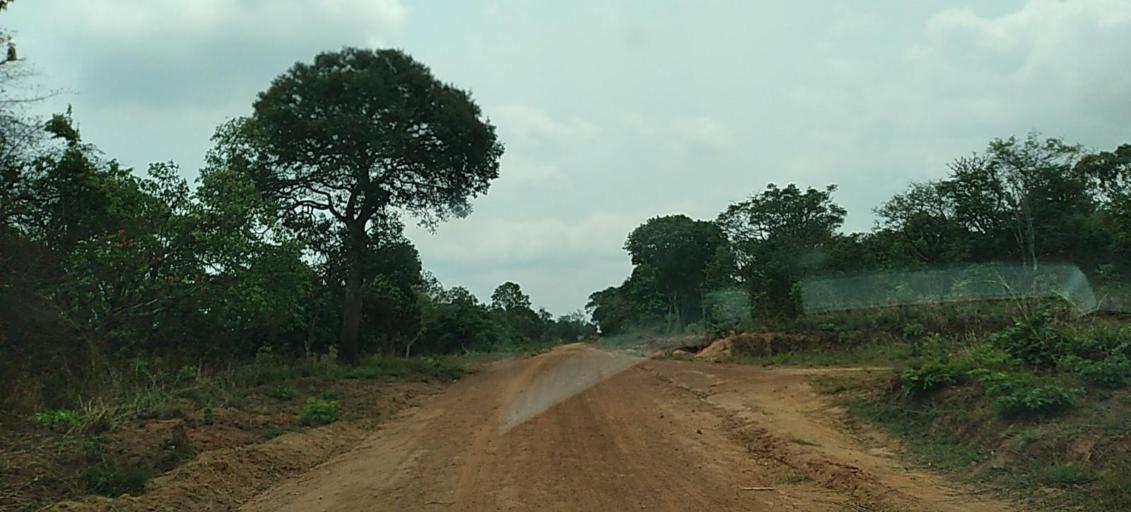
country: ZM
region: North-Western
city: Mwinilunga
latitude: -11.4537
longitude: 24.7550
